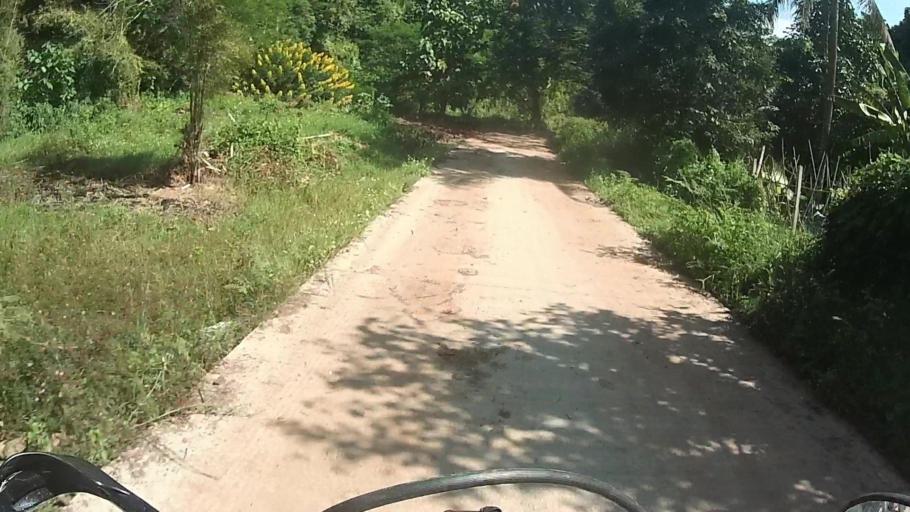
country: TH
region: Chiang Mai
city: Mae Taeng
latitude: 19.0040
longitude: 98.8672
